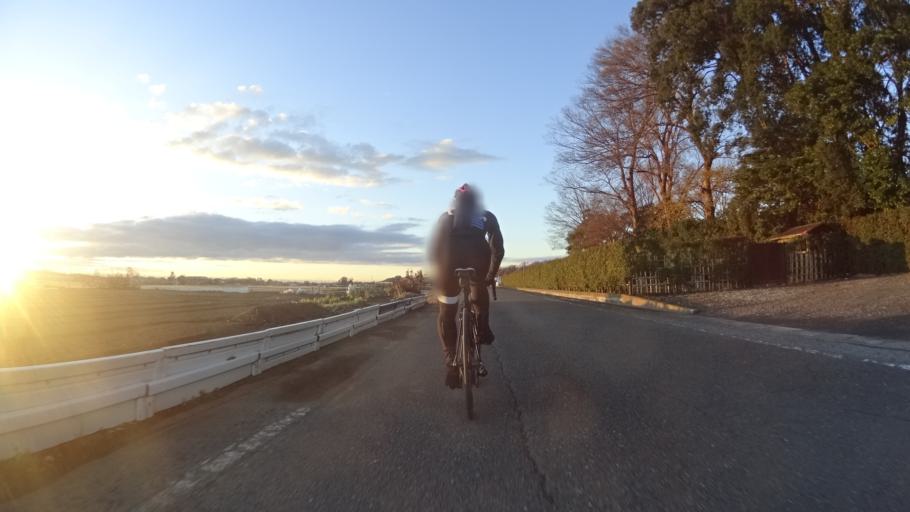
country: JP
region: Kanagawa
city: Zama
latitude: 35.5142
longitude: 139.3684
